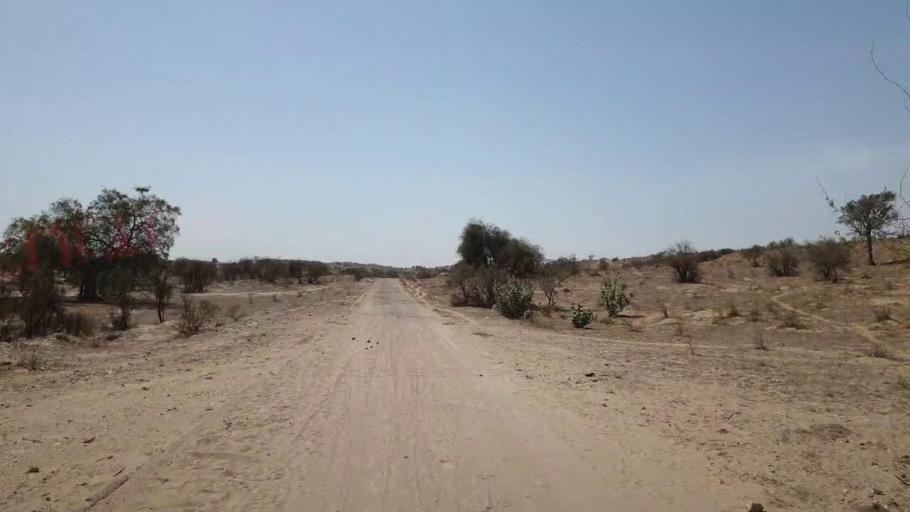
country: PK
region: Sindh
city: Umarkot
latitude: 25.2218
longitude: 69.9436
